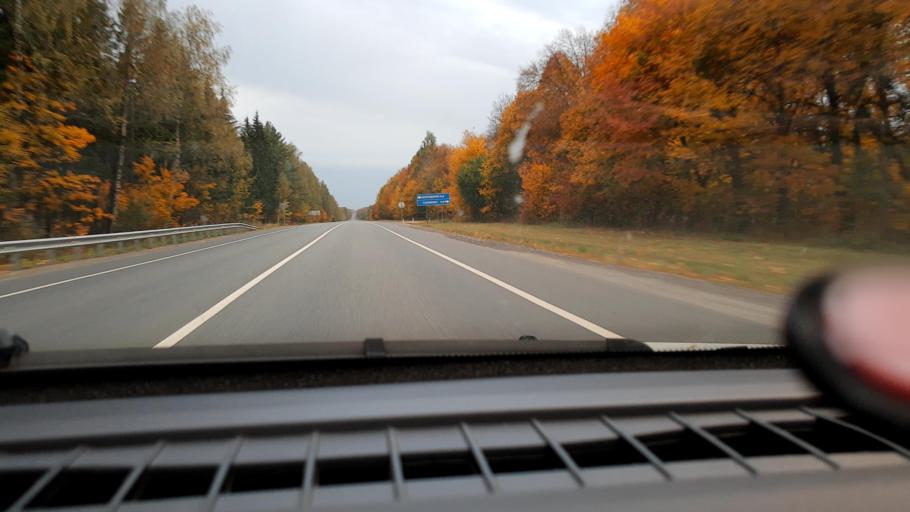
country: RU
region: Vladimir
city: Orgtrud
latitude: 56.1999
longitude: 40.8160
